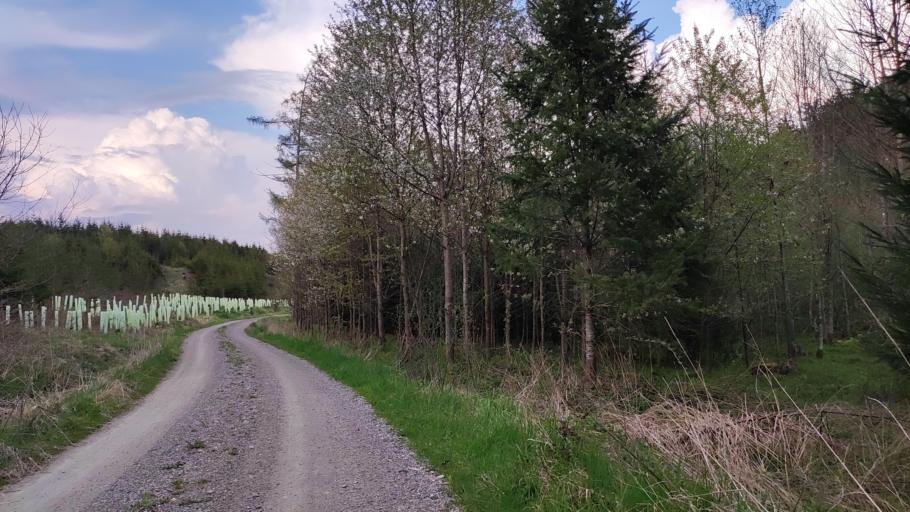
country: DE
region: Bavaria
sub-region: Swabia
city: Zusmarshausen
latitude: 48.3935
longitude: 10.5584
